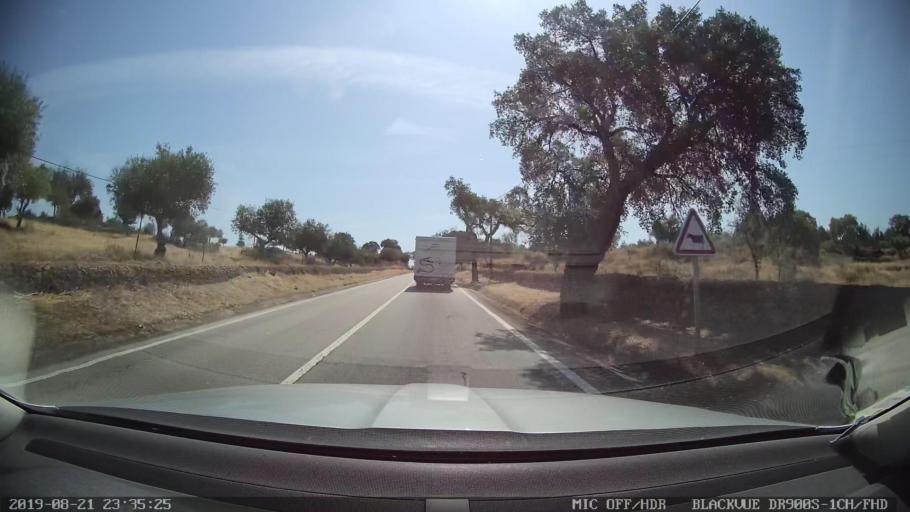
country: PT
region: Guarda
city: Alcains
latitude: 39.8784
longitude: -7.3882
